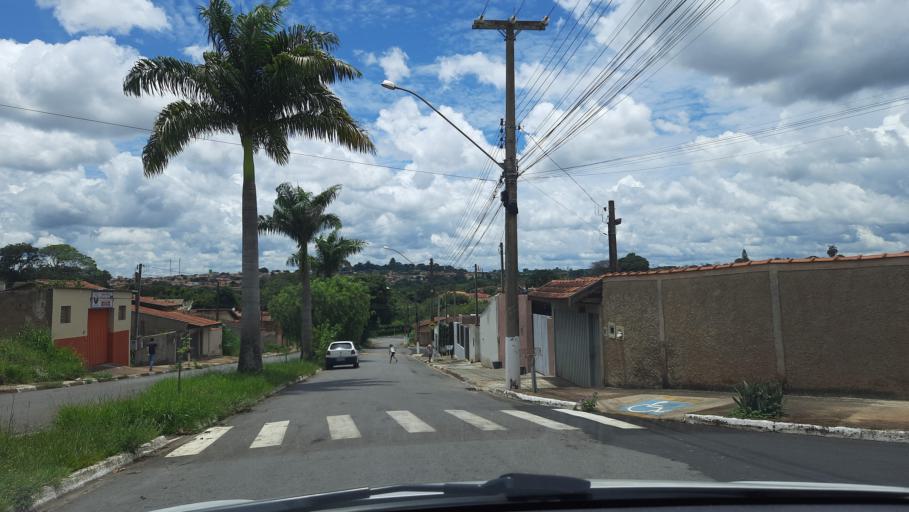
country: BR
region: Sao Paulo
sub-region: Casa Branca
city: Casa Branca
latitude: -21.7831
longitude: -47.0940
